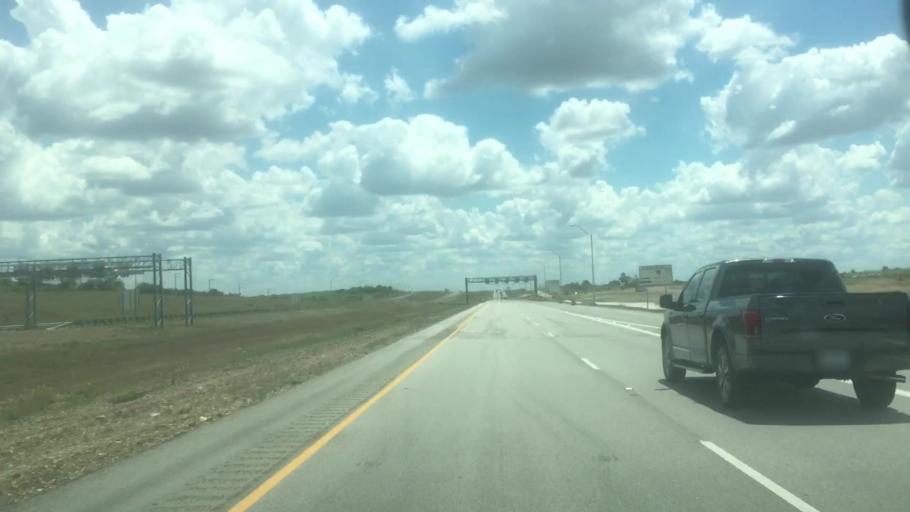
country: US
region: Texas
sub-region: Caldwell County
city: Uhland
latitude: 29.9922
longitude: -97.6848
